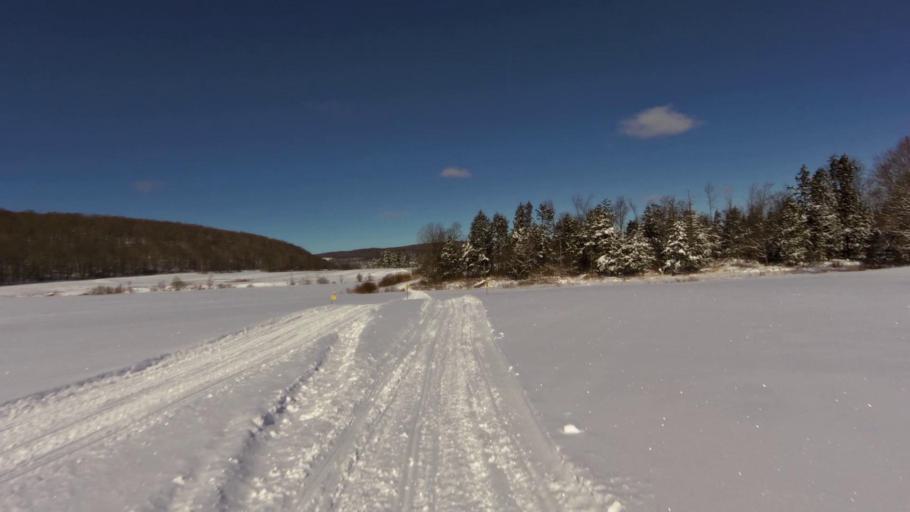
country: US
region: New York
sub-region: Chautauqua County
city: Fredonia
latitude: 42.3490
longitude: -79.1733
